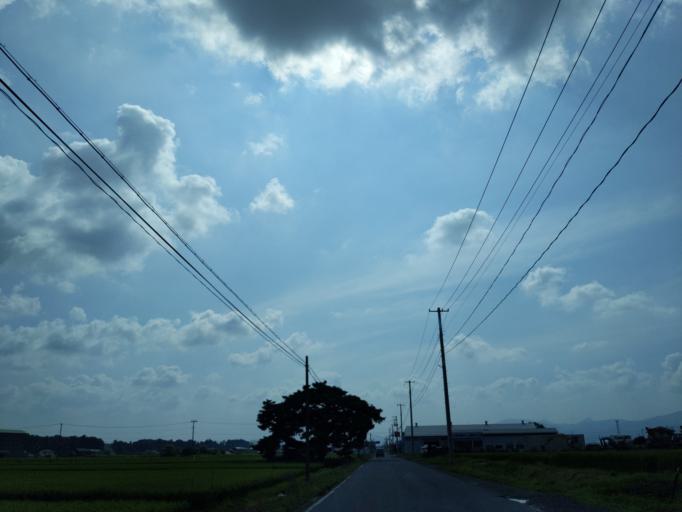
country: JP
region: Fukushima
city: Koriyama
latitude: 37.3651
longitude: 140.3445
